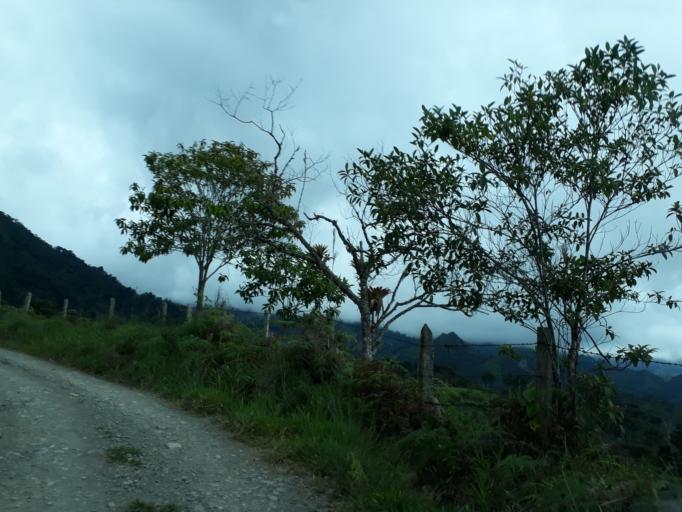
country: CO
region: Boyaca
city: Muzo
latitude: 5.3841
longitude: -74.1015
